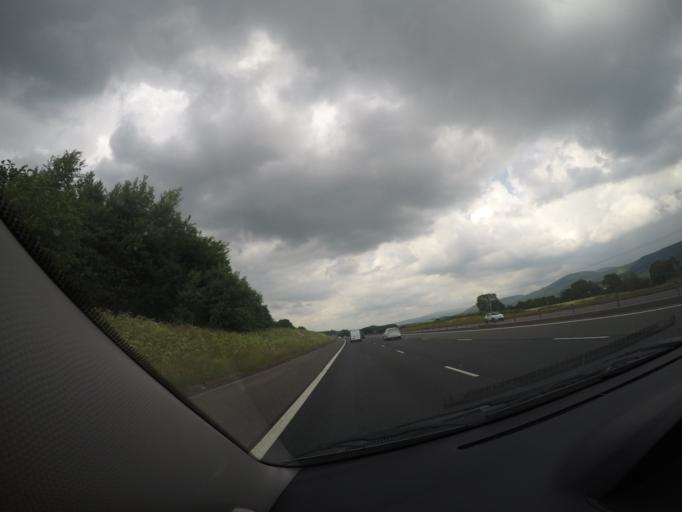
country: GB
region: Scotland
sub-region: Dumfries and Galloway
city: Moffat
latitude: 55.2537
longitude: -3.4111
